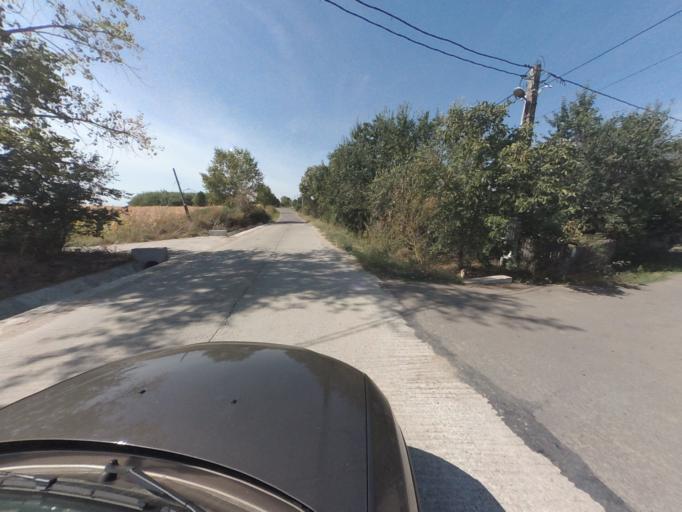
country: RO
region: Vaslui
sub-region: Comuna Deleni
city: Deleni
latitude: 46.5435
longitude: 27.7555
